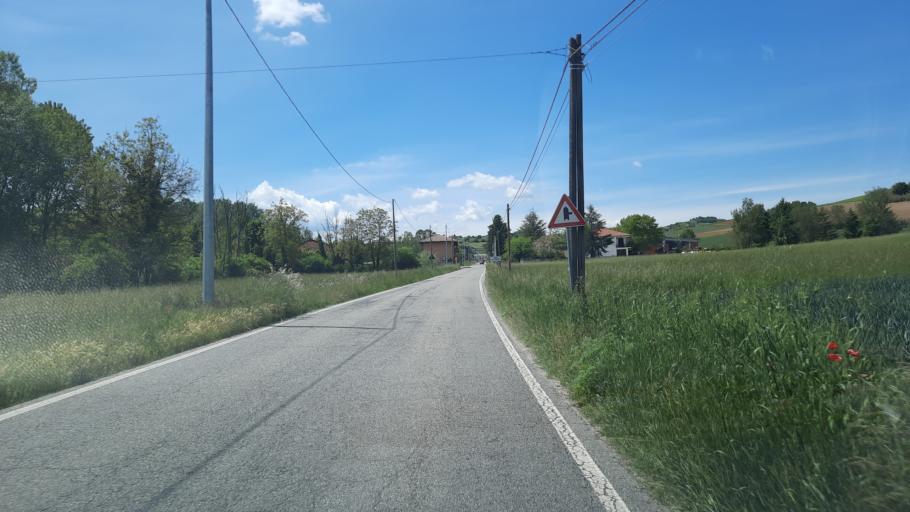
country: IT
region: Piedmont
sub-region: Provincia di Alessandria
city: Castelletto Merli
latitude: 45.0629
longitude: 8.2514
